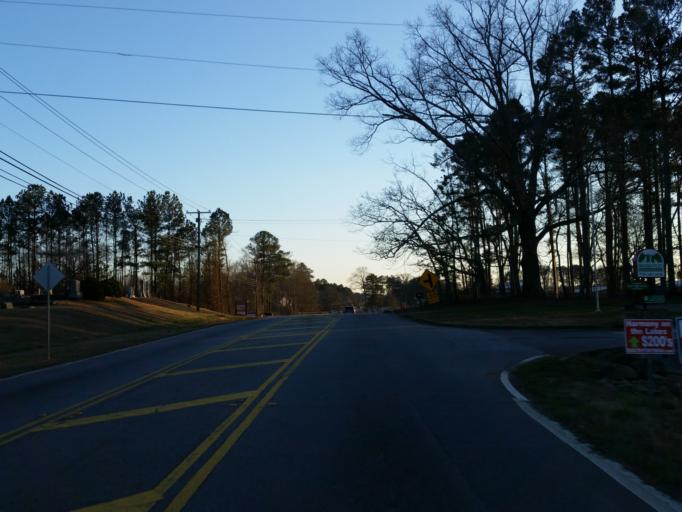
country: US
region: Georgia
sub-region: Cherokee County
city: Holly Springs
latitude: 34.1750
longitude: -84.4209
